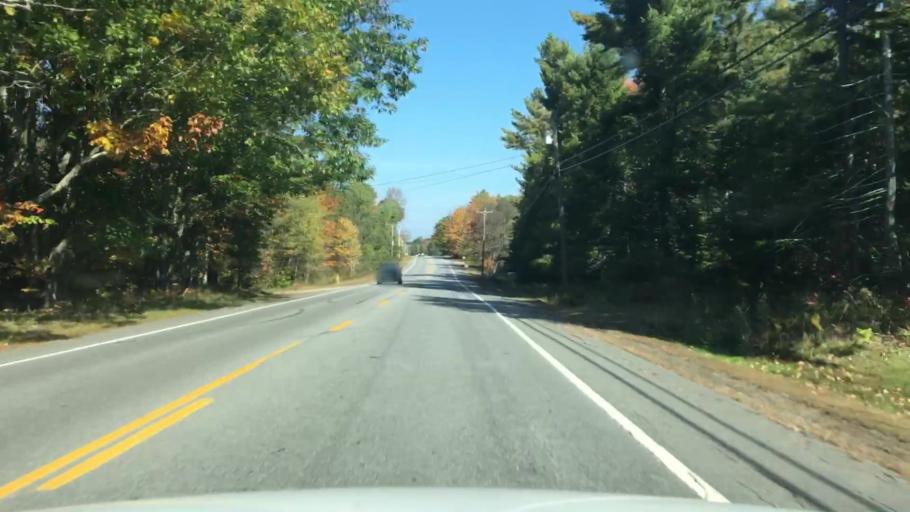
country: US
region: Maine
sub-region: Sagadahoc County
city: Topsham
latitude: 44.0181
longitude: -69.9441
